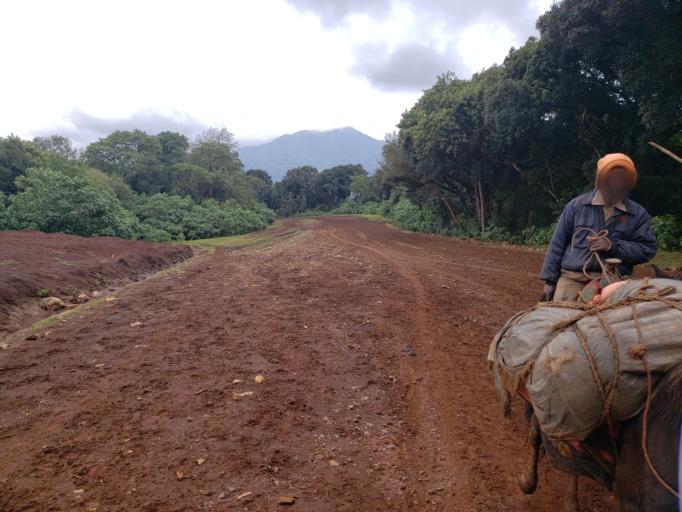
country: ET
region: Oromiya
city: Dodola
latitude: 6.6142
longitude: 39.4198
